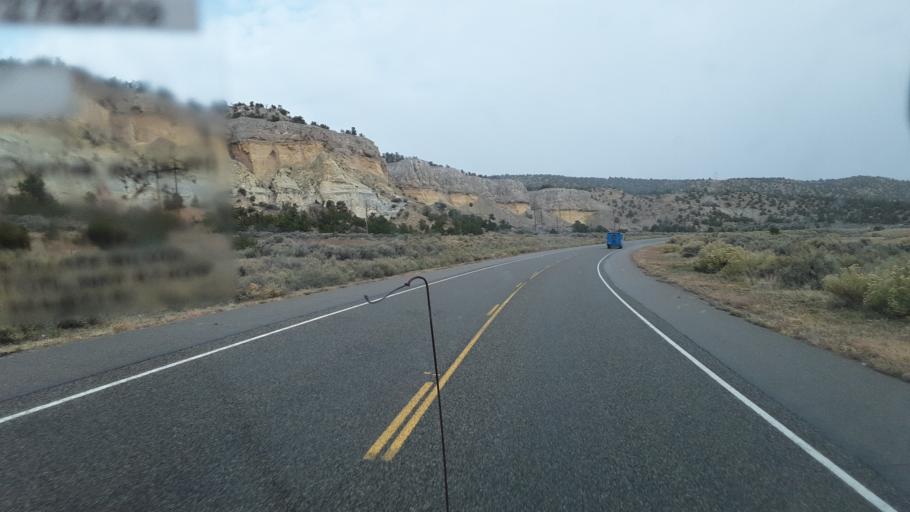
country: US
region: New Mexico
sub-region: Rio Arriba County
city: Santa Teresa
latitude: 36.3804
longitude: -106.5043
